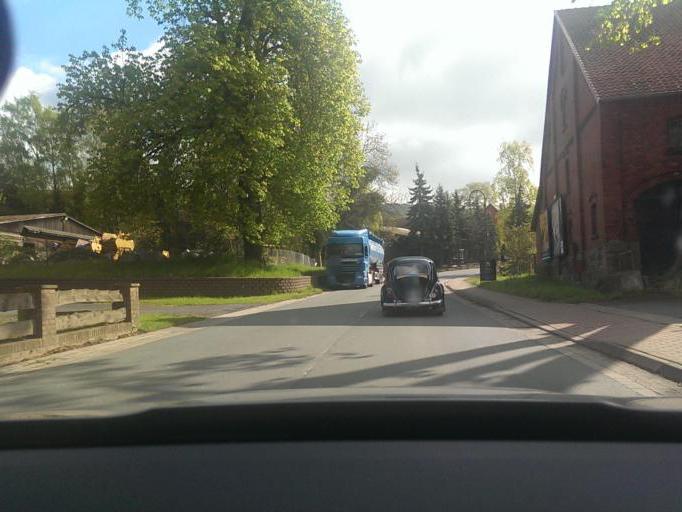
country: DE
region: Lower Saxony
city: Hameln
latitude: 52.1596
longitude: 9.3539
